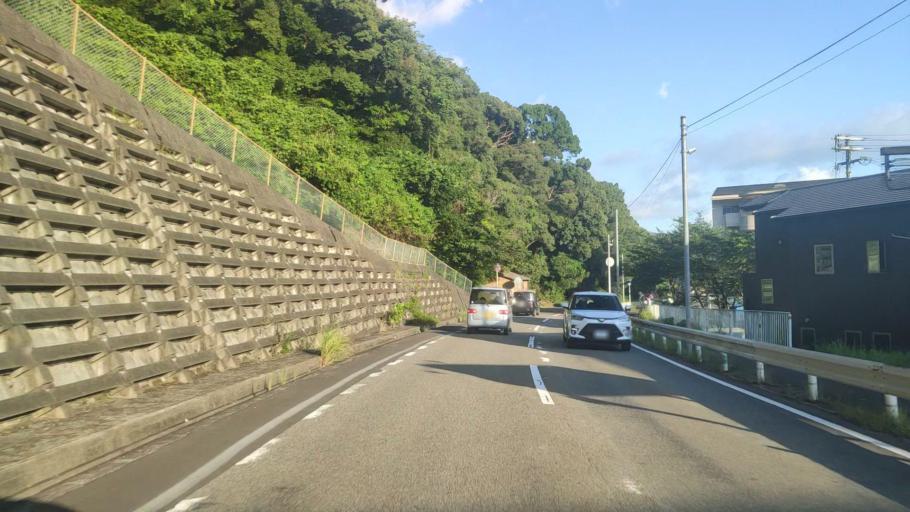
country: JP
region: Wakayama
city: Tanabe
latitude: 33.7251
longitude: 135.4443
